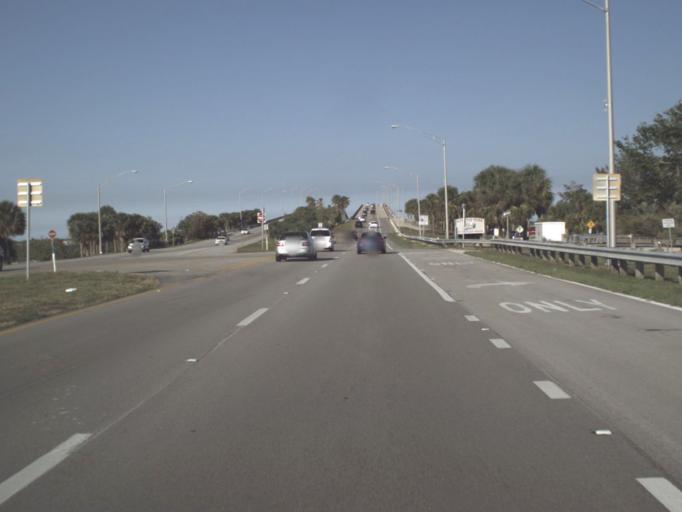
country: US
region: Florida
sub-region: Brevard County
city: Melbourne
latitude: 28.0815
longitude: -80.5986
